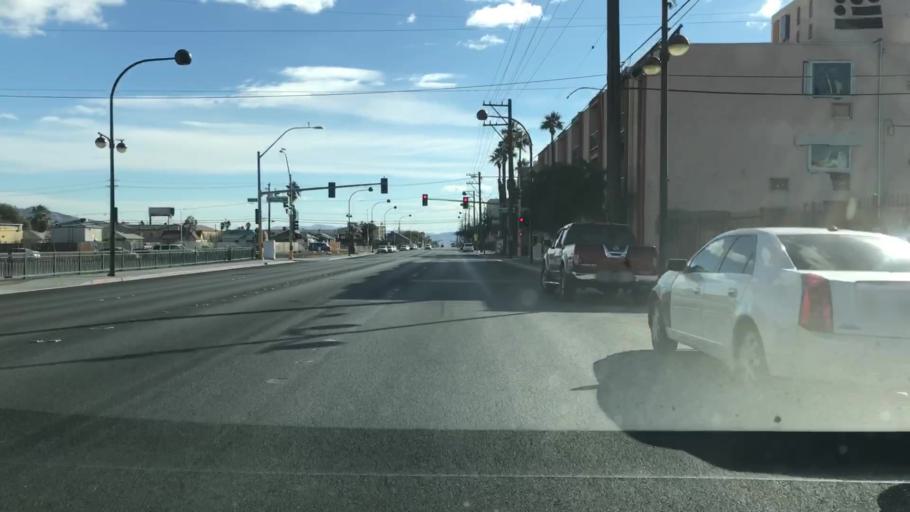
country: US
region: Nevada
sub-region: Clark County
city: Las Vegas
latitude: 36.1709
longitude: -115.1378
